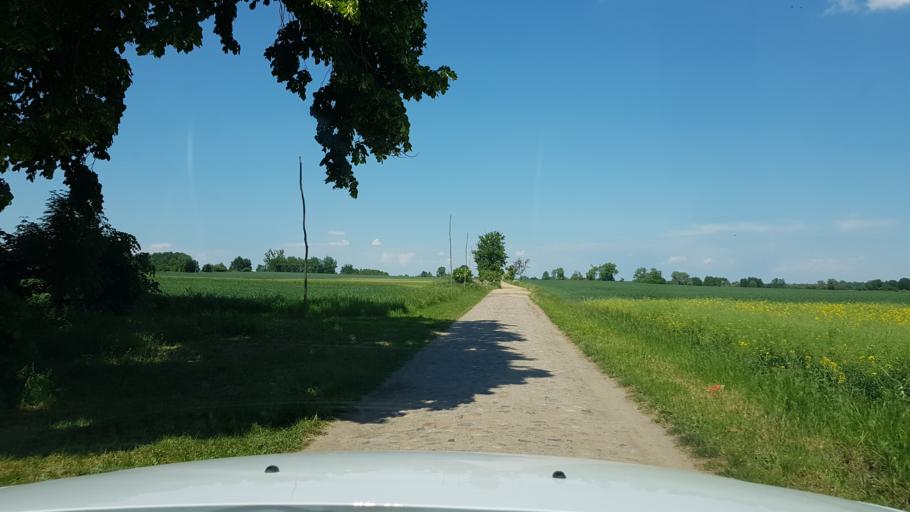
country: PL
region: West Pomeranian Voivodeship
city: Trzcinsko Zdroj
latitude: 52.9450
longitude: 14.5808
